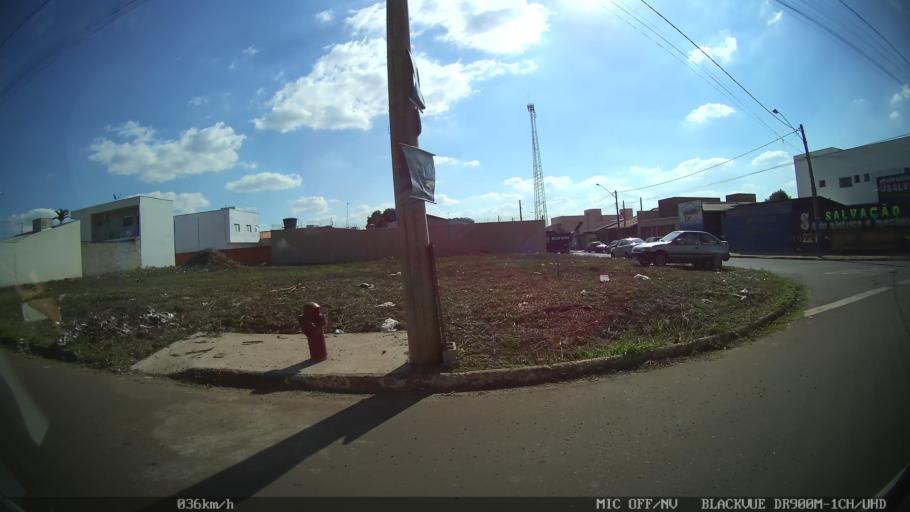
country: BR
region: Sao Paulo
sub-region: Sumare
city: Sumare
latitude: -22.8215
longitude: -47.2903
